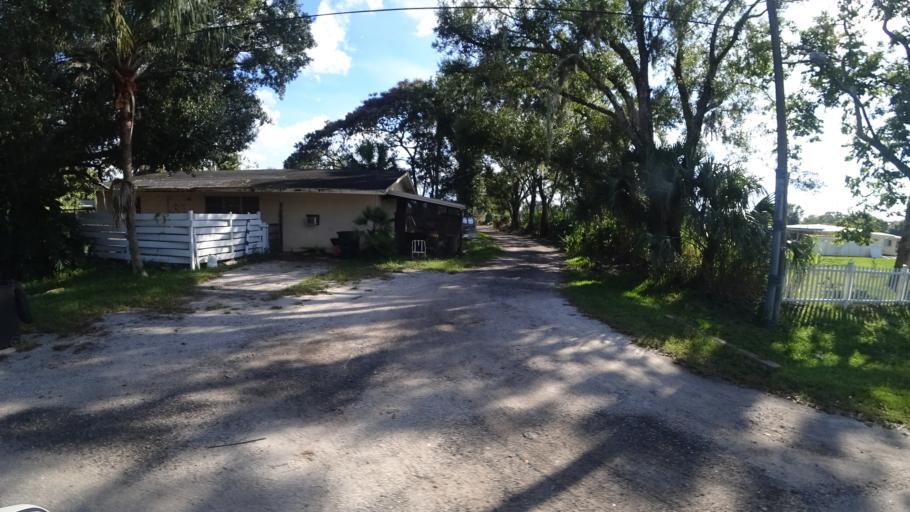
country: US
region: Florida
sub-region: Manatee County
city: Ellenton
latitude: 27.4830
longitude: -82.4870
